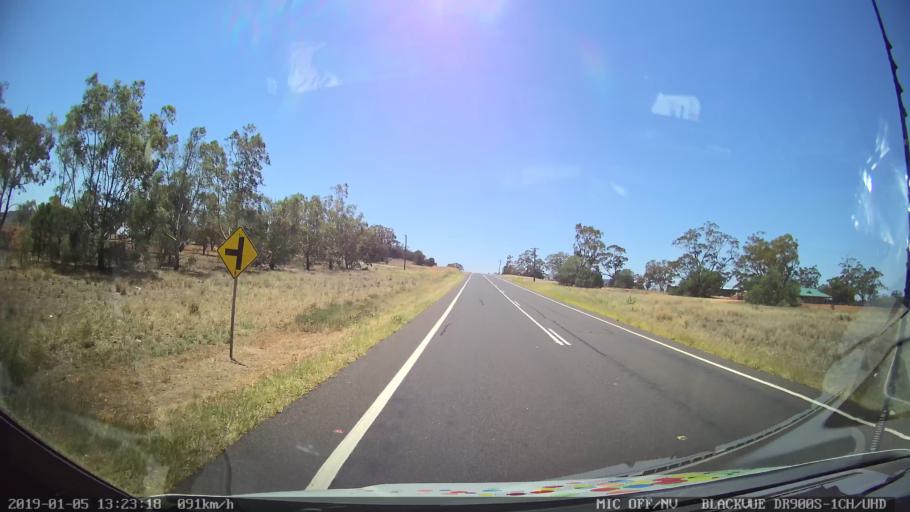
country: AU
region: New South Wales
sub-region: Gunnedah
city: Gunnedah
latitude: -31.0790
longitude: 149.9735
